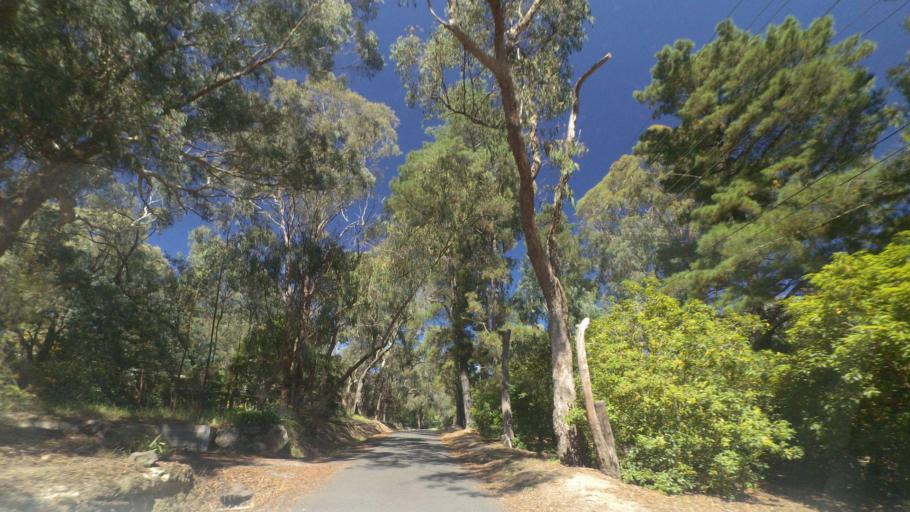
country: AU
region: Victoria
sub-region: Manningham
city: Donvale
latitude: -37.7881
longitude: 145.1909
